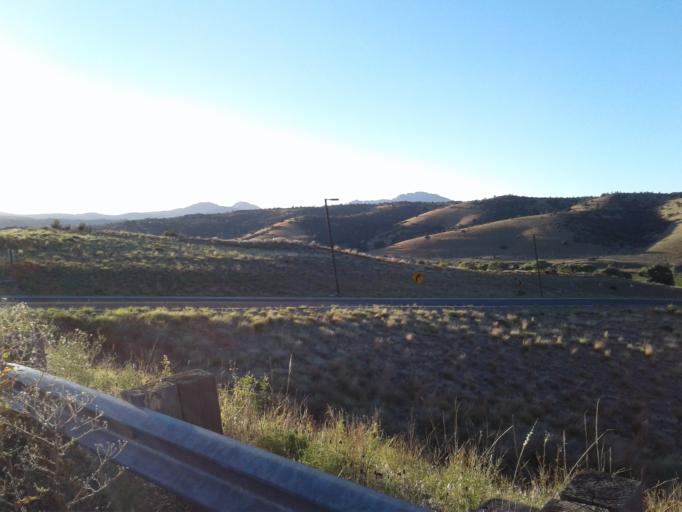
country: US
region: Arizona
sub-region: Yavapai County
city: Prescott
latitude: 34.5537
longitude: -112.4475
